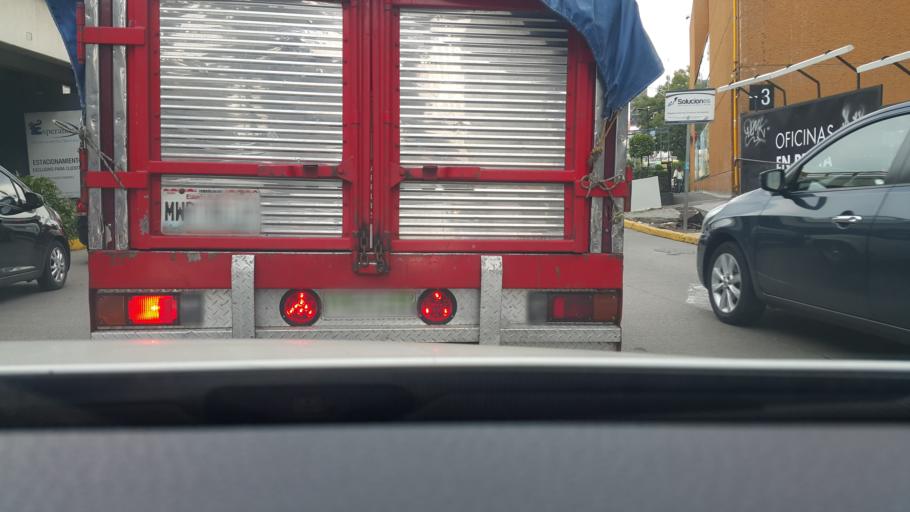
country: MX
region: Mexico City
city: Coyoacan
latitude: 19.3590
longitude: -99.1701
